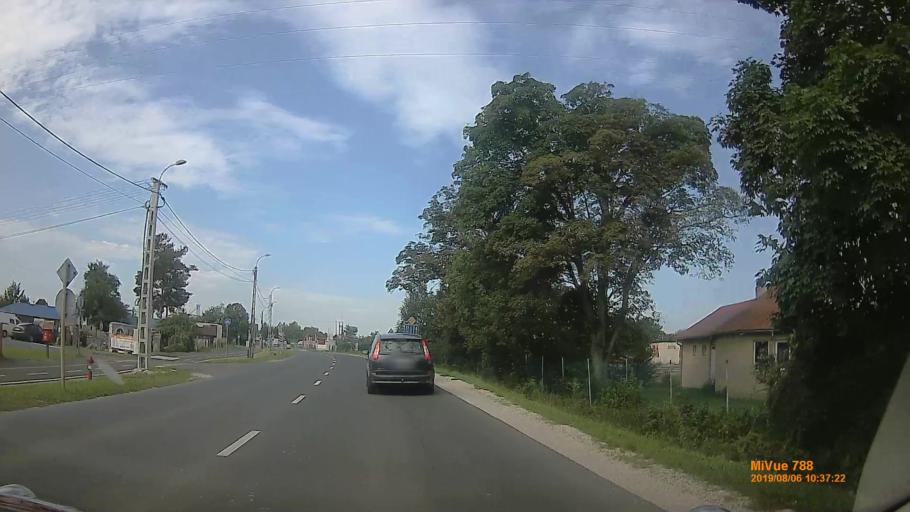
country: HU
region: Vas
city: Kormend
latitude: 47.0096
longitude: 16.5787
